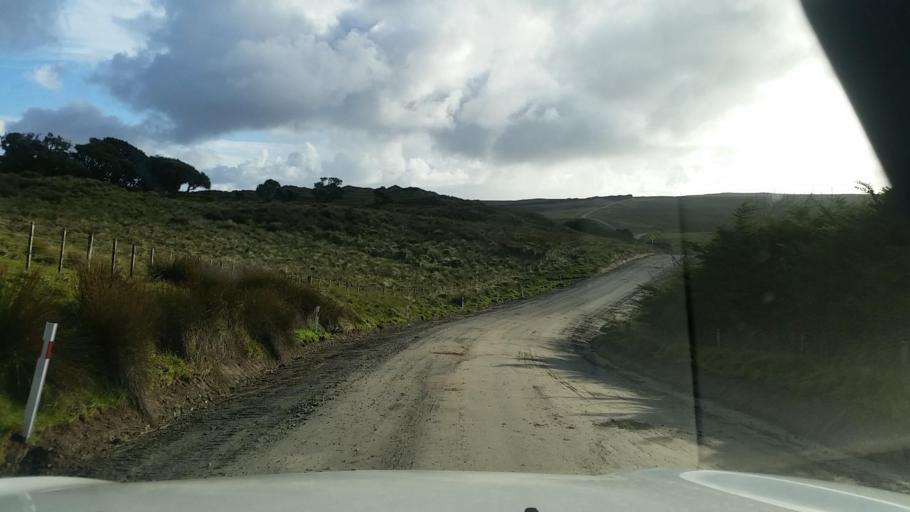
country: NZ
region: Chatham Islands
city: Waitangi
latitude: -43.8092
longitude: -176.5992
